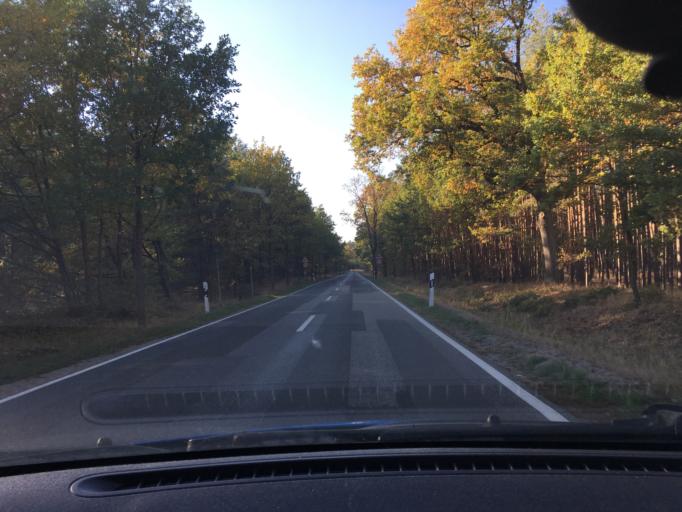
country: DE
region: Lower Saxony
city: Damnatz
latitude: 53.1604
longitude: 11.1919
